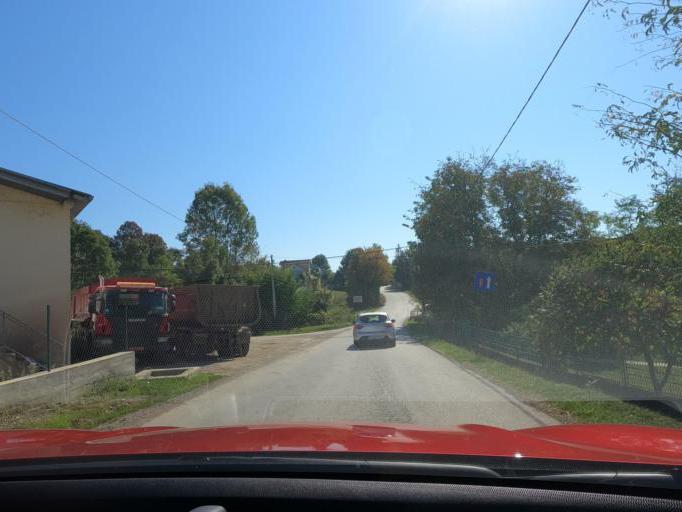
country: RS
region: Central Serbia
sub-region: Raski Okrug
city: Kraljevo
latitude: 43.7648
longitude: 20.6727
